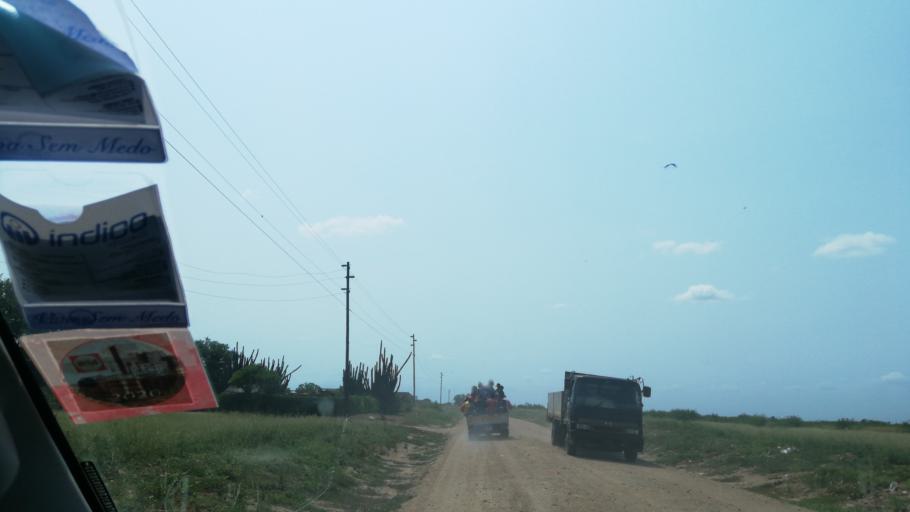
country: MZ
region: Maputo
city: Matola
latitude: -26.0644
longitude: 32.3903
